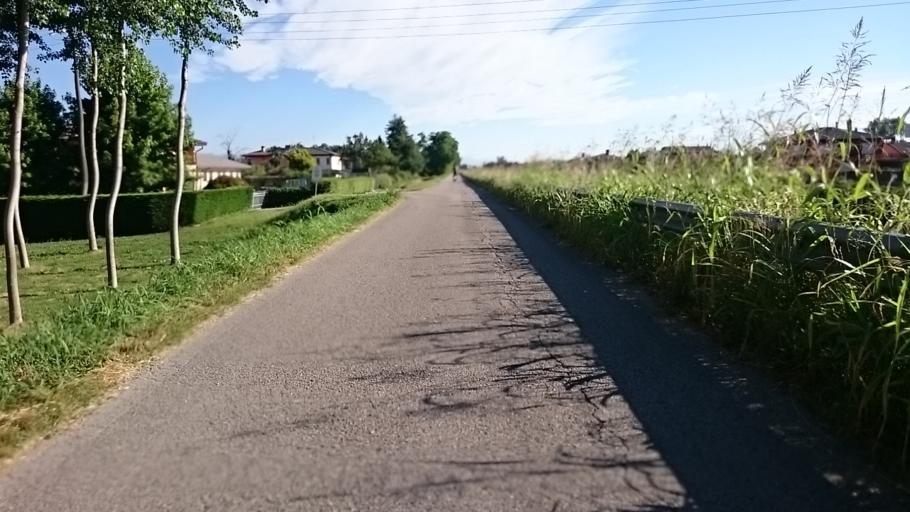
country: IT
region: Veneto
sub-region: Provincia di Padova
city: Campodarsego
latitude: 45.5144
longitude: 11.9111
